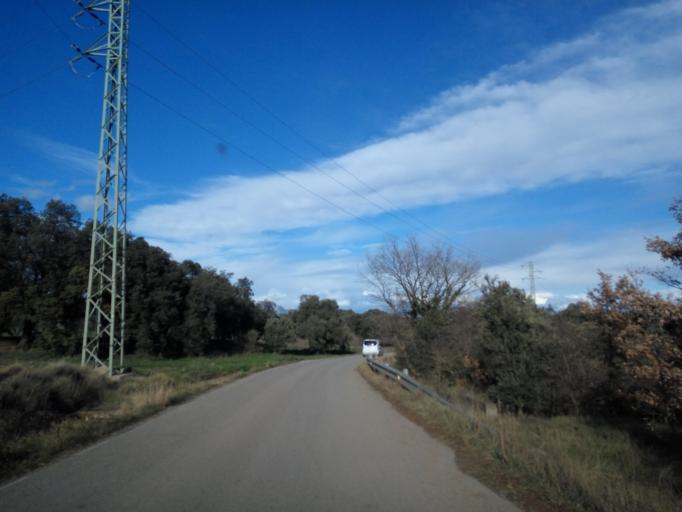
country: ES
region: Catalonia
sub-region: Provincia de Barcelona
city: Capolat
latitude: 42.0296
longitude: 1.7850
